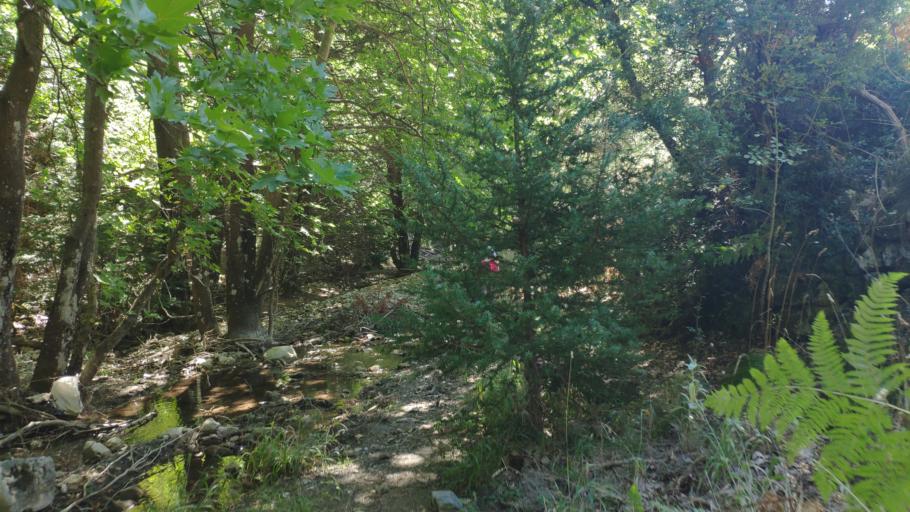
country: GR
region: Peloponnese
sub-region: Nomos Lakonias
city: Kariai
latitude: 37.1743
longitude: 22.5833
